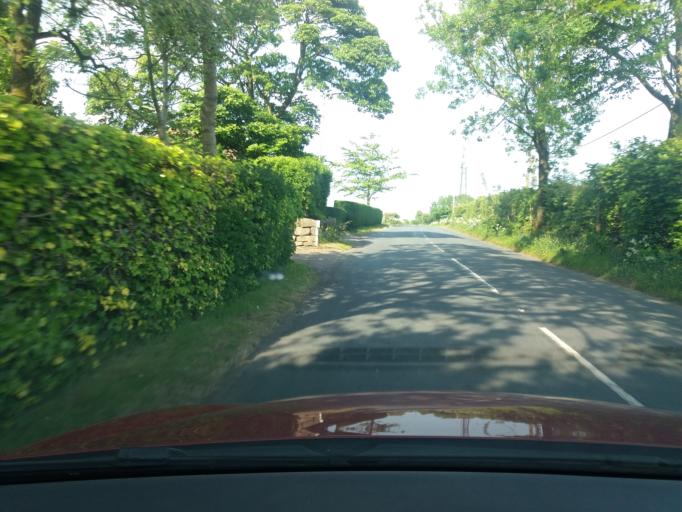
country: GB
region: England
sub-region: Lancashire
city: Chorley
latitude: 53.6865
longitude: -2.5836
